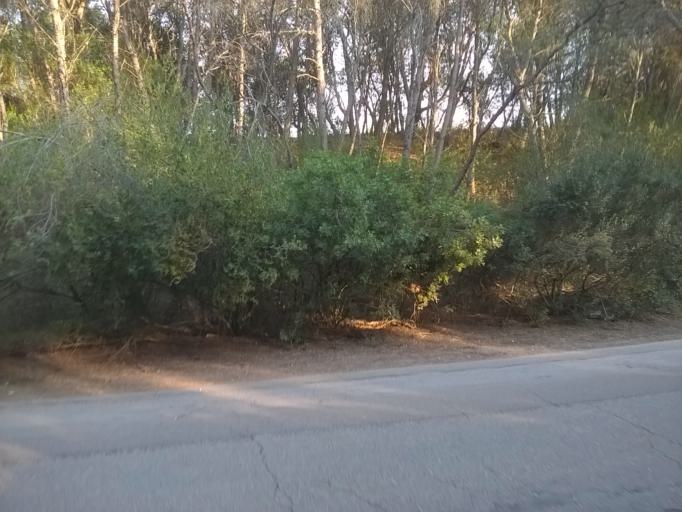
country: IT
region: Apulia
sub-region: Provincia di Taranto
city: Marina di Ginosa
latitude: 40.4704
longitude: 16.9457
